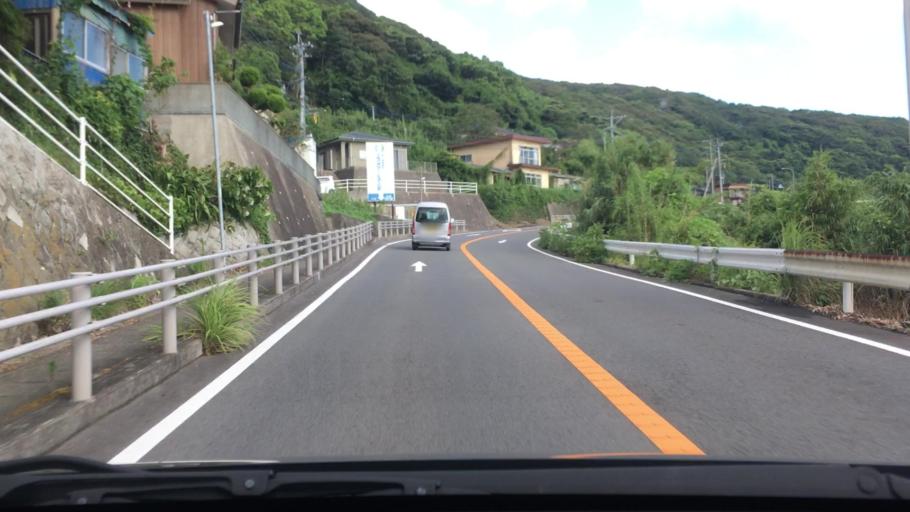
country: JP
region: Nagasaki
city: Togitsu
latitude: 32.8304
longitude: 129.7230
